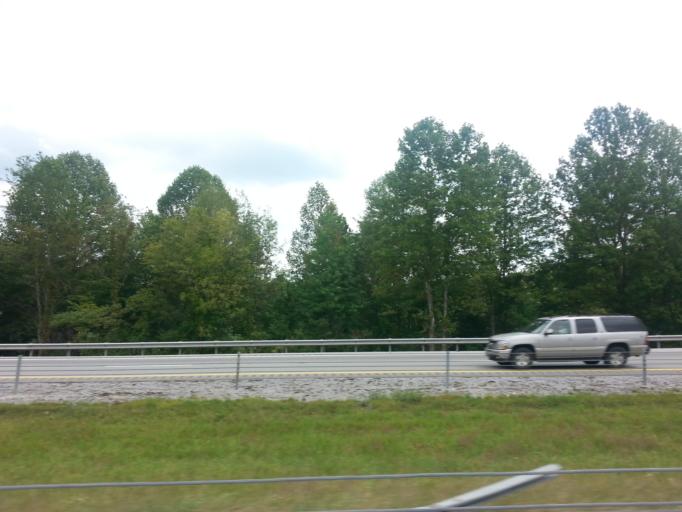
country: US
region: Tennessee
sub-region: Roane County
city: Rockwood
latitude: 35.8955
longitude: -84.7968
